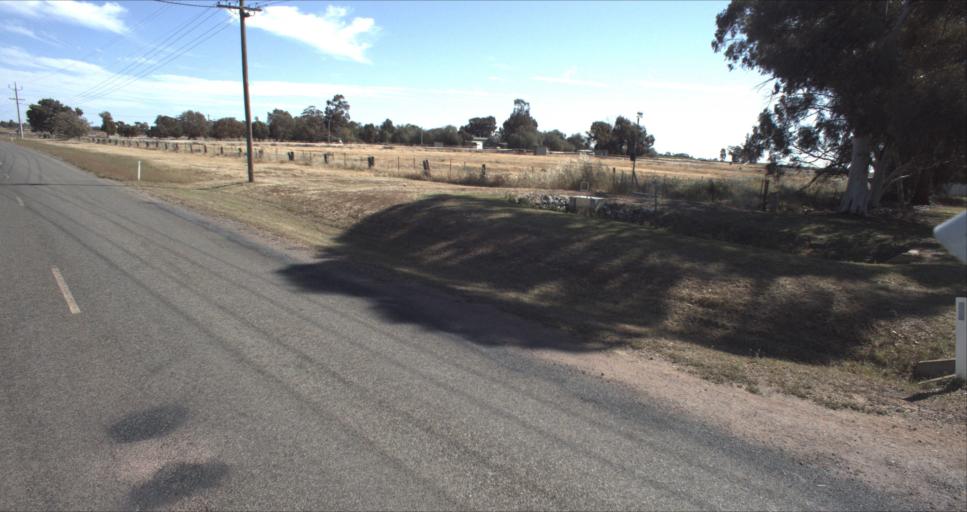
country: AU
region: New South Wales
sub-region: Leeton
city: Leeton
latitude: -34.5649
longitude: 146.3828
